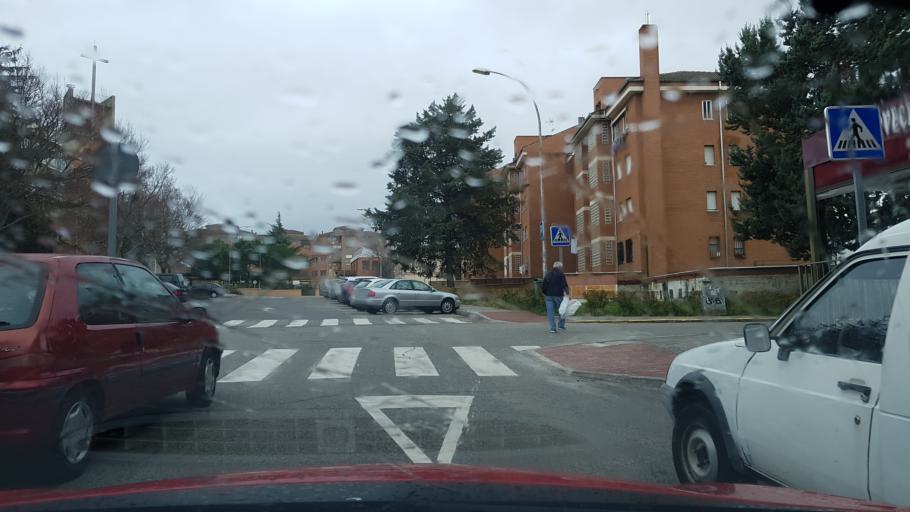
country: ES
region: Castille and Leon
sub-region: Provincia de Segovia
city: Segovia
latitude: 40.9423
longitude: -4.1058
